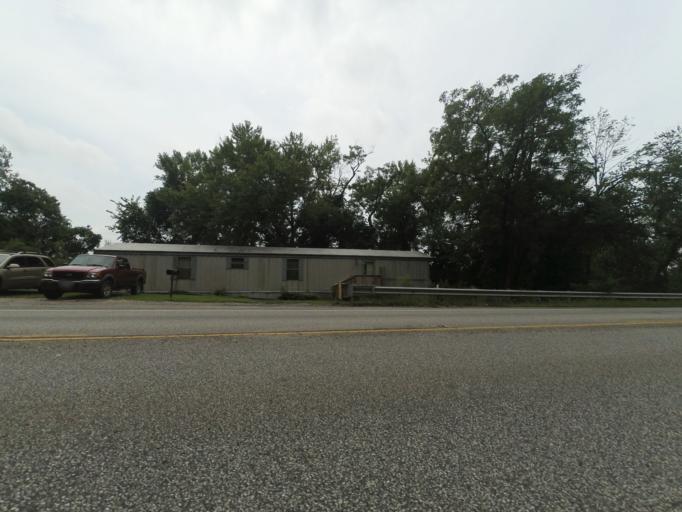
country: US
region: West Virginia
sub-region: Cabell County
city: Huntington
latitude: 38.4356
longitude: -82.4214
